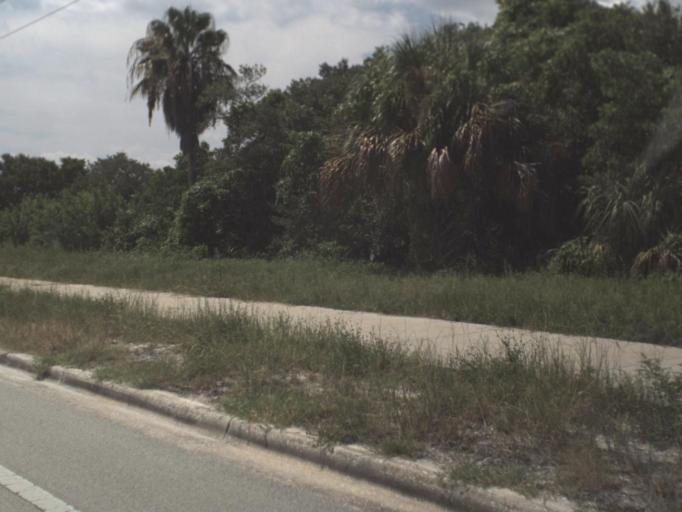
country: US
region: Florida
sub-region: Pinellas County
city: Tierra Verde
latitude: 27.6606
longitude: -82.7229
